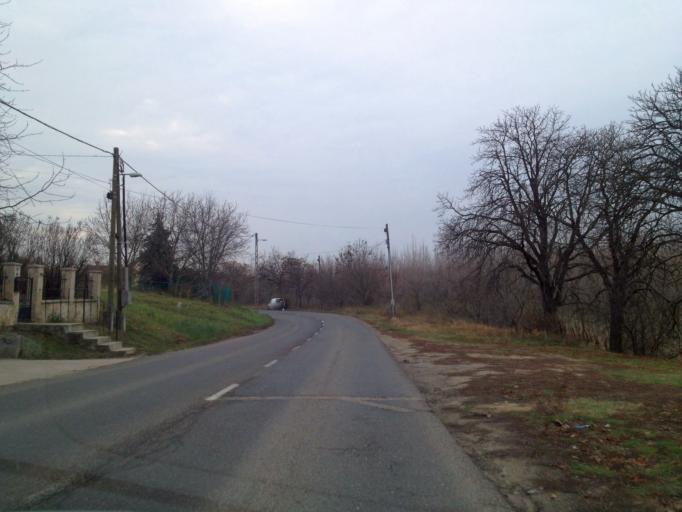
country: HU
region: Heves
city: Hatvan
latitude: 47.6863
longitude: 19.6902
